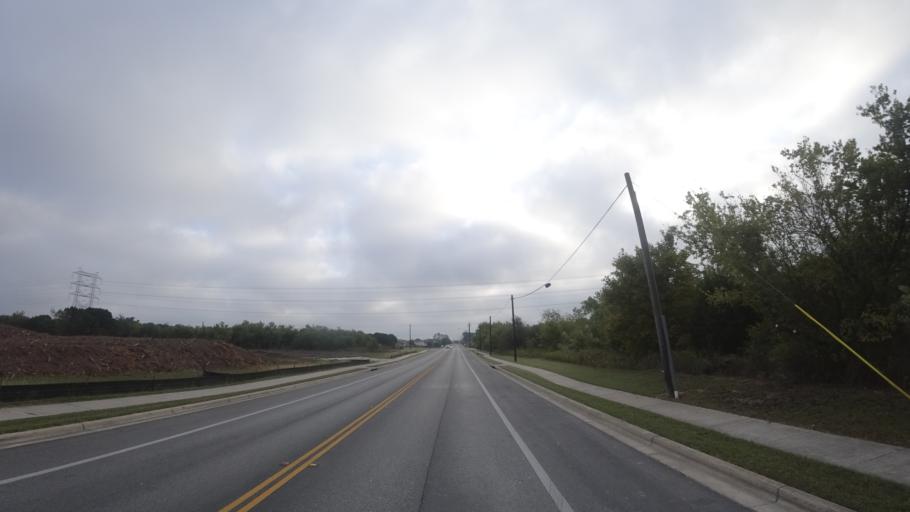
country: US
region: Texas
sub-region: Travis County
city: Pflugerville
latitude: 30.3593
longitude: -97.6485
